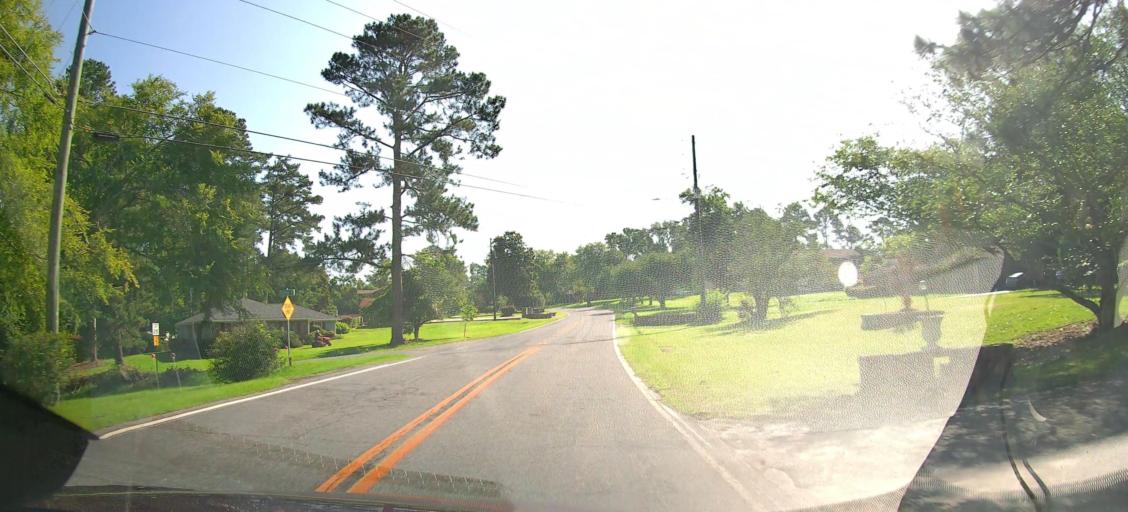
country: US
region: Georgia
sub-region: Peach County
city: Byron
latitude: 32.7283
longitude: -83.7088
